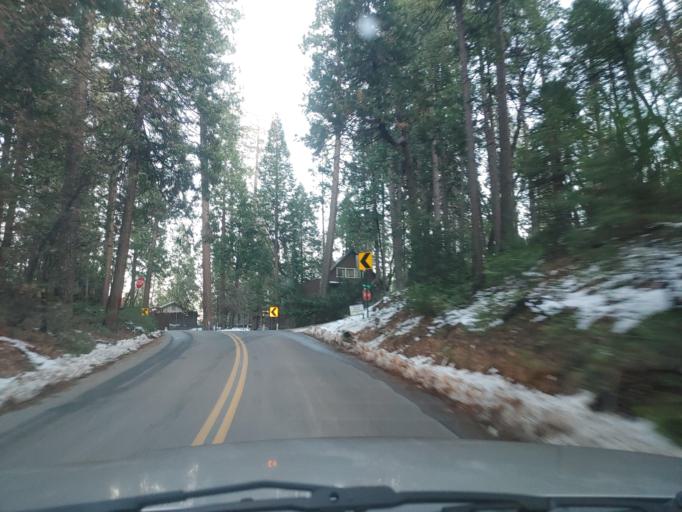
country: US
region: California
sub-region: Tuolumne County
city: Twain Harte
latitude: 38.0367
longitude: -120.2381
